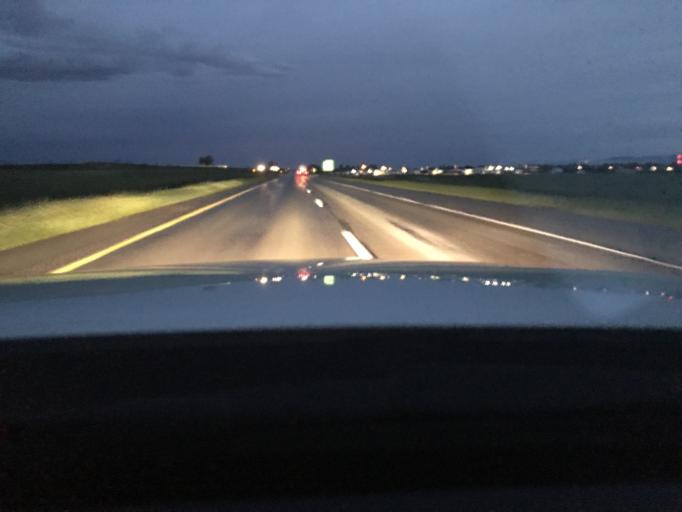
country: US
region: Colorado
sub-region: Larimer County
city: Wellington
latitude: 40.7223
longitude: -104.9939
